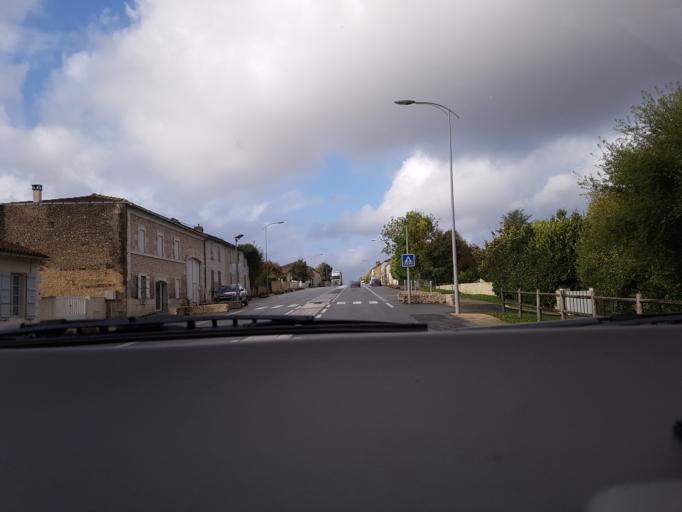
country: FR
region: Poitou-Charentes
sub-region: Departement de la Charente-Maritime
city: Les Gonds
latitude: 45.6518
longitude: -0.5866
